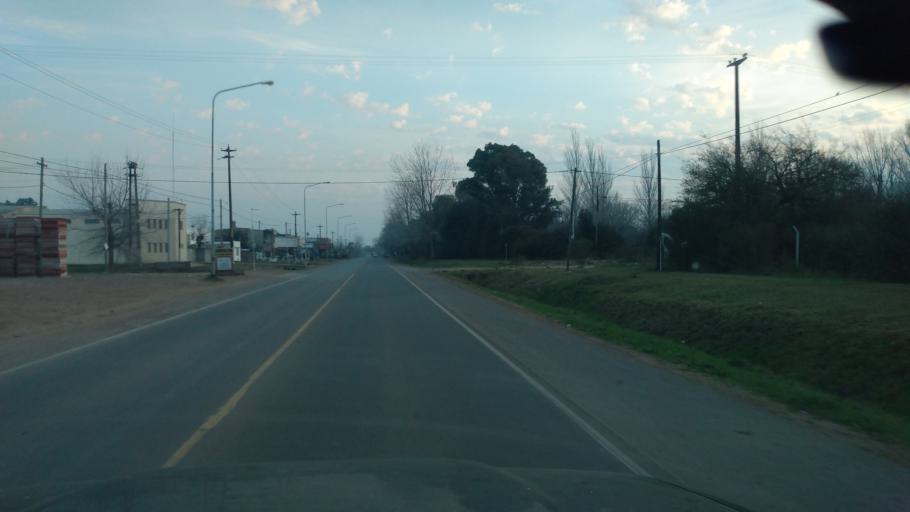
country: AR
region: Buenos Aires
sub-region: Partido de Lujan
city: Lujan
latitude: -34.5599
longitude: -59.1331
